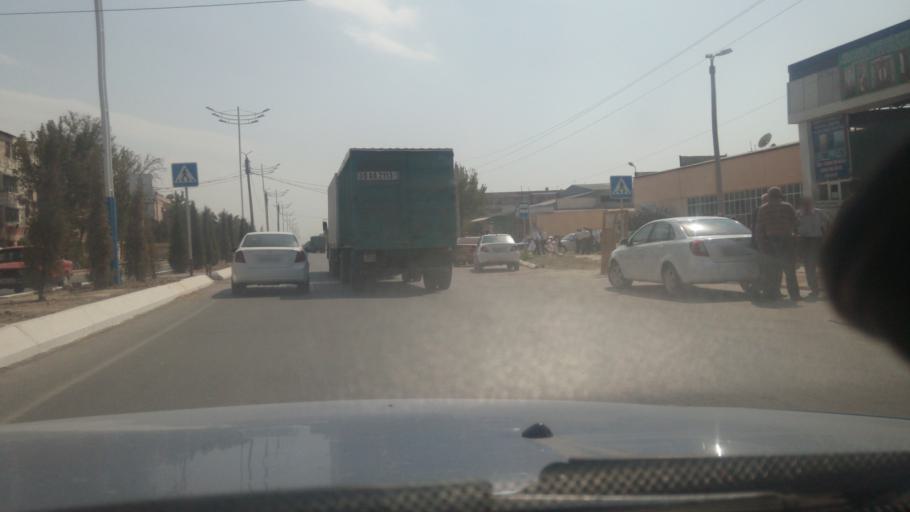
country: UZ
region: Sirdaryo
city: Guliston
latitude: 40.5166
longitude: 68.7690
